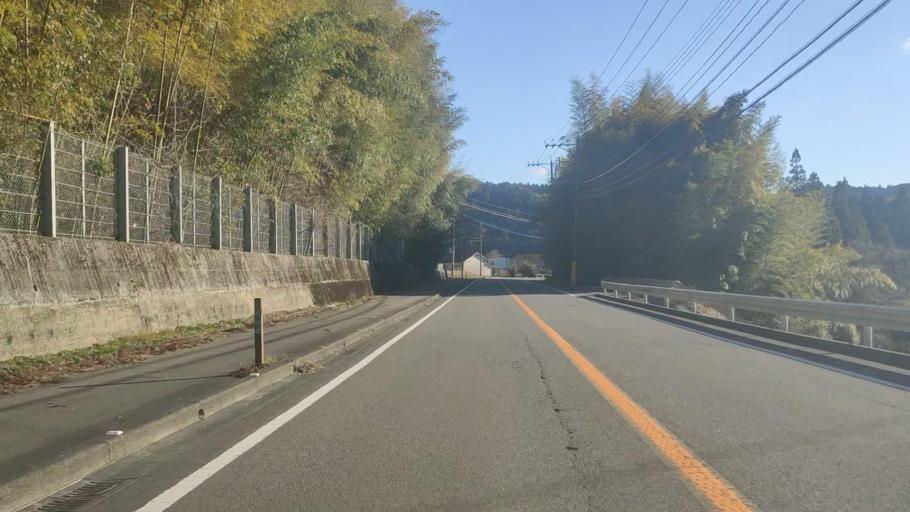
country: JP
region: Fukuoka
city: Maebaru-chuo
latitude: 33.4549
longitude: 130.2756
